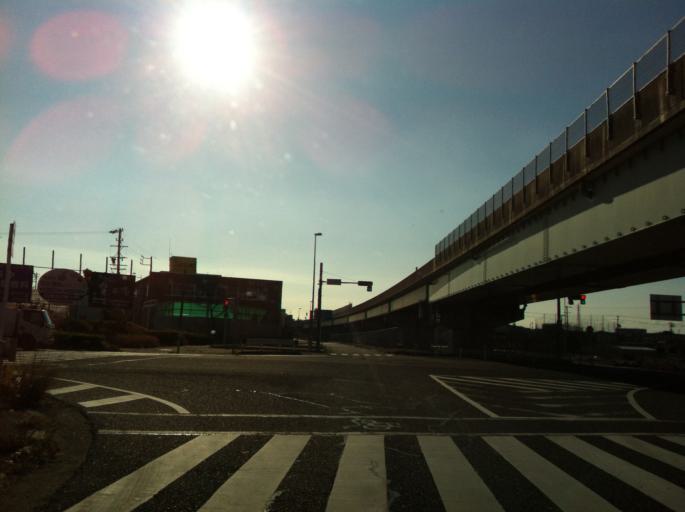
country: JP
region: Aichi
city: Toyohashi
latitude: 34.7081
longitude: 137.3534
